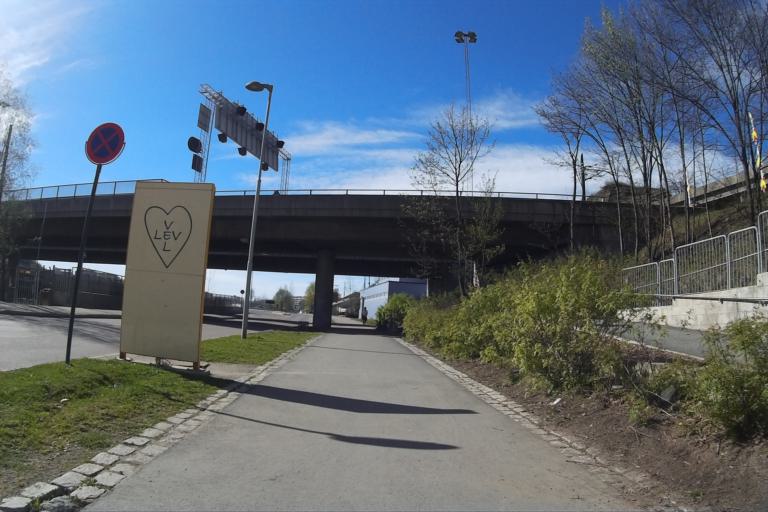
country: NO
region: Oslo
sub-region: Oslo
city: Oslo
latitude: 59.9048
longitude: 10.7859
